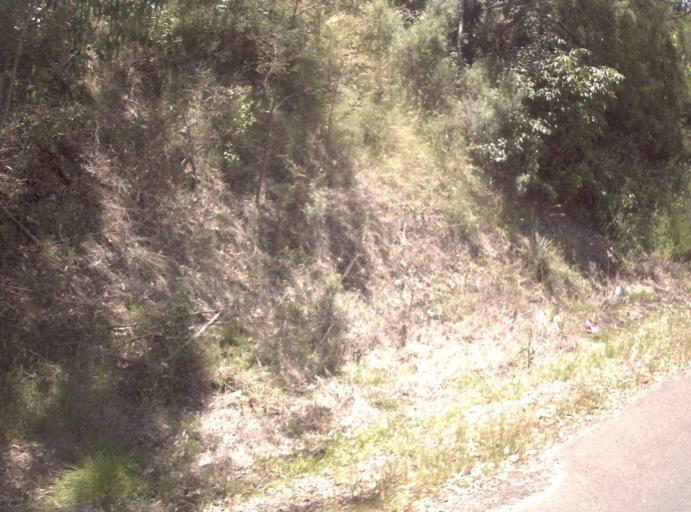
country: AU
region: Victoria
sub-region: East Gippsland
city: Lakes Entrance
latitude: -37.8484
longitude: 148.0399
